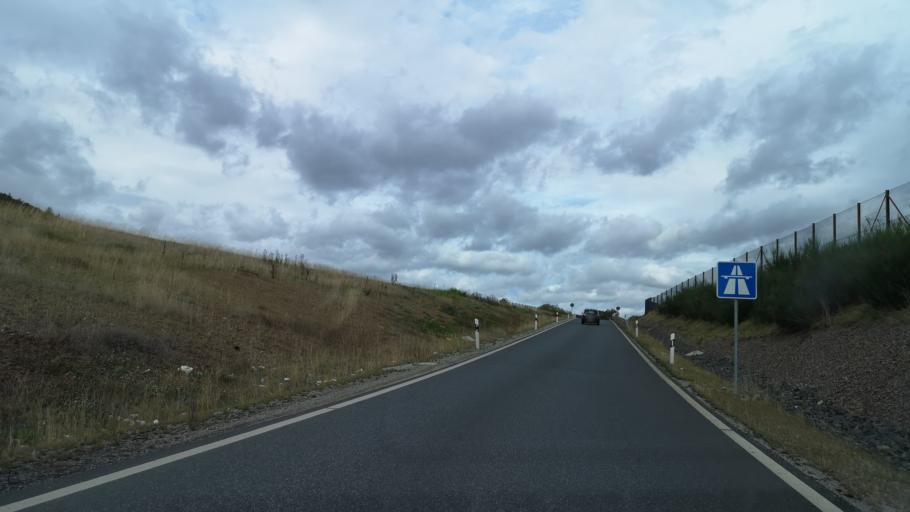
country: DE
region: Hesse
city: Waldkappel
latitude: 51.1462
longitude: 9.9225
